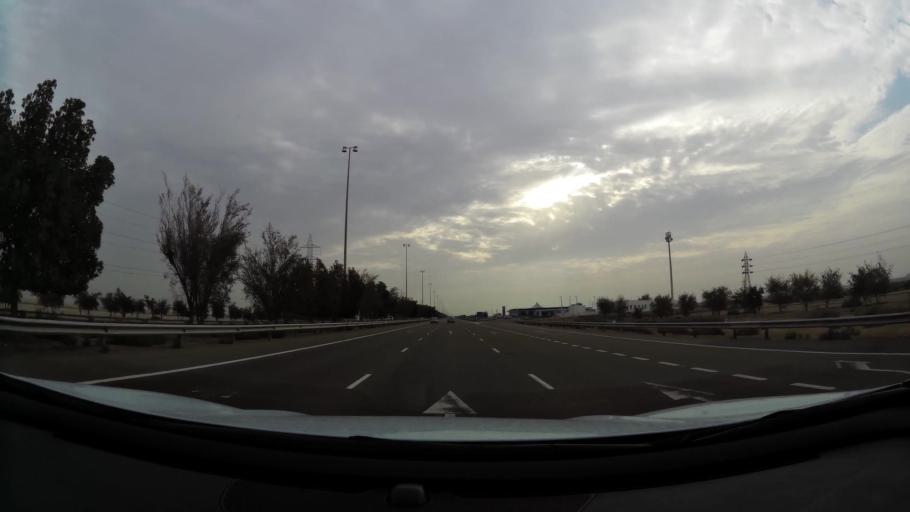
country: AE
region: Abu Dhabi
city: Abu Dhabi
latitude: 24.2188
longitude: 54.8500
